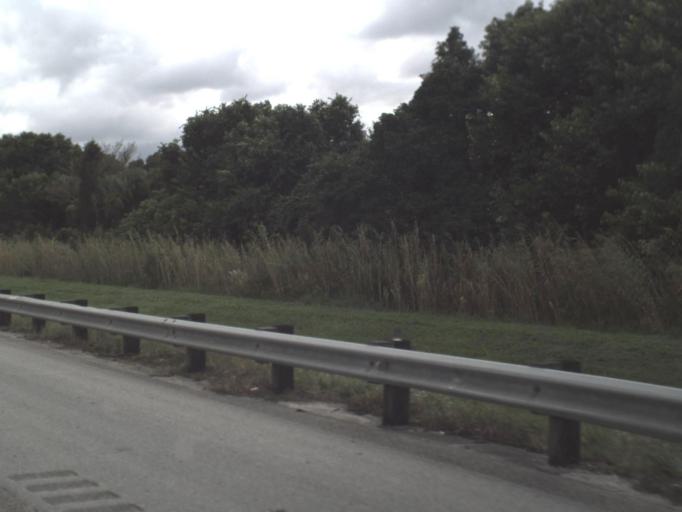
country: US
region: Florida
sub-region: Palm Beach County
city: Palm Beach Gardens
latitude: 26.8206
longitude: -80.1308
